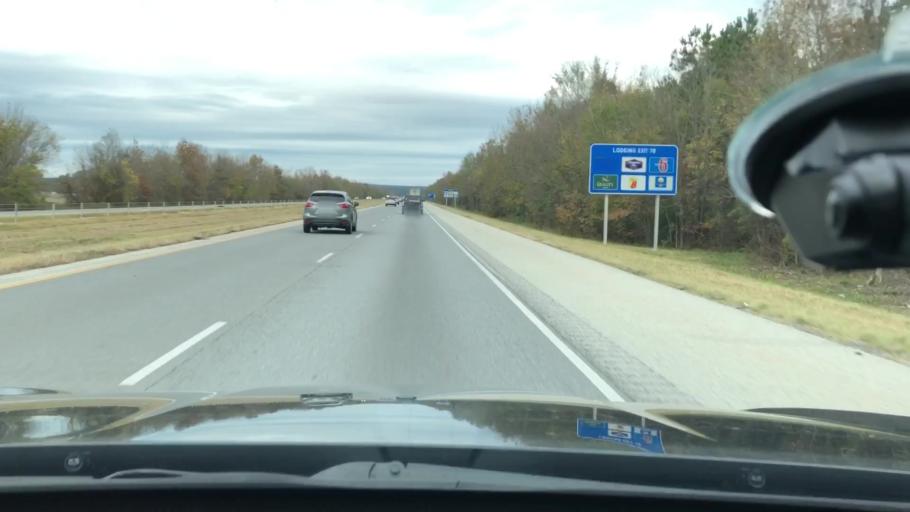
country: US
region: Arkansas
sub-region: Clark County
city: Arkadelphia
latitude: 34.1588
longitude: -93.0771
